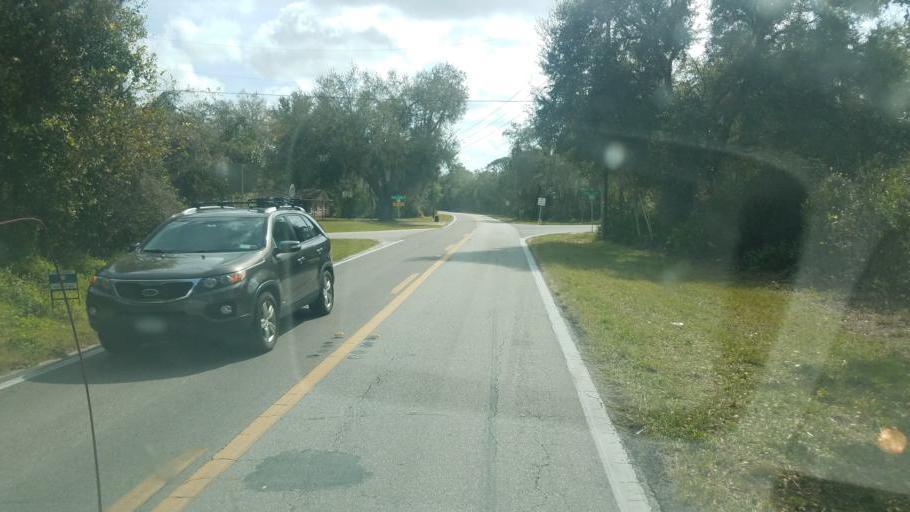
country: US
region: Florida
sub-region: Polk County
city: Dundee
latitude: 27.9809
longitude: -81.5499
